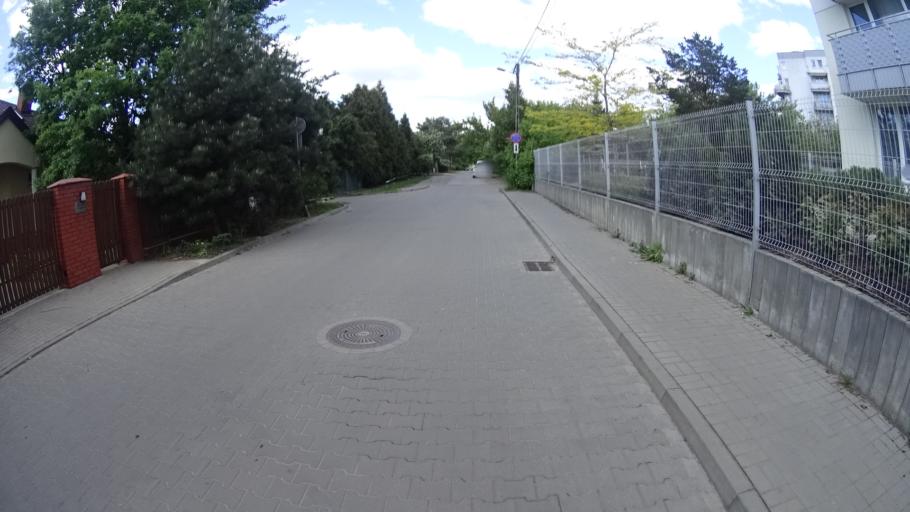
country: PL
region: Masovian Voivodeship
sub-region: Warszawa
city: Bemowo
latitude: 52.2733
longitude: 20.9125
